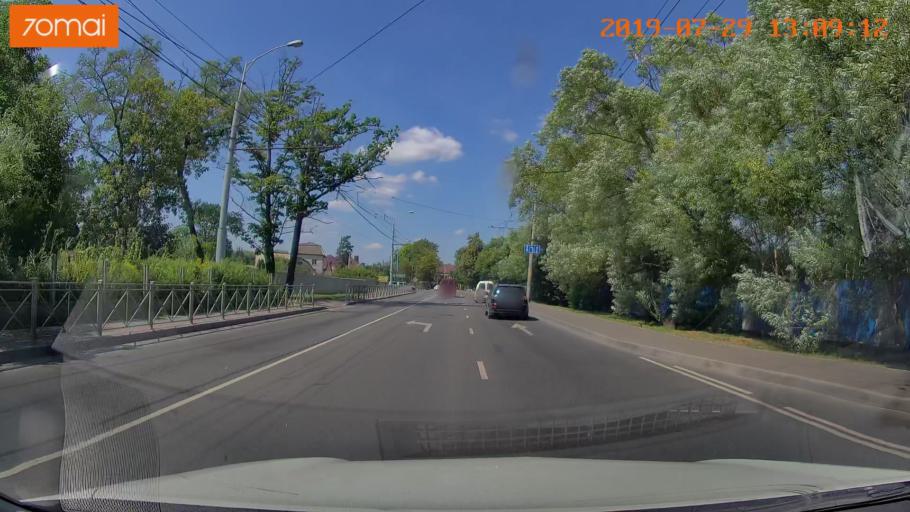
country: RU
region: Kaliningrad
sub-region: Gorod Kaliningrad
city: Kaliningrad
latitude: 54.7133
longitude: 20.4205
